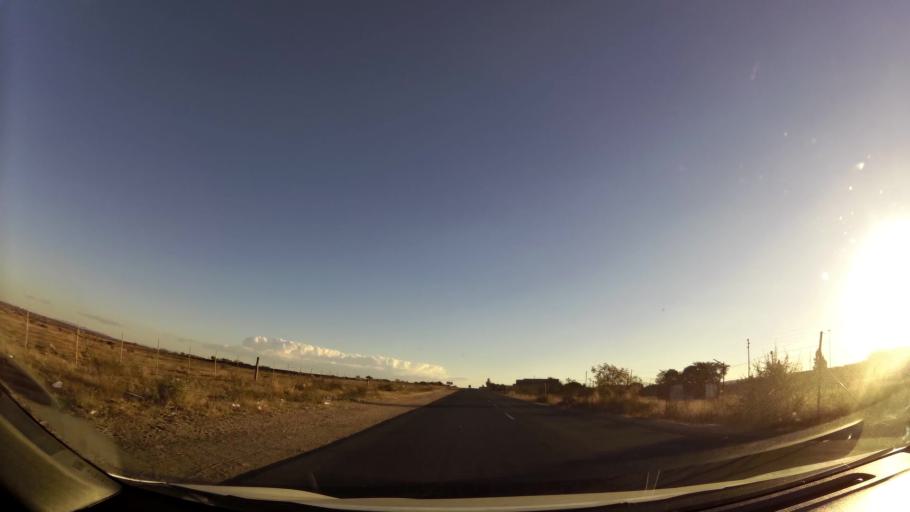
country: ZA
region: Limpopo
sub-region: Capricorn District Municipality
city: Polokwane
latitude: -23.8322
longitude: 29.3703
